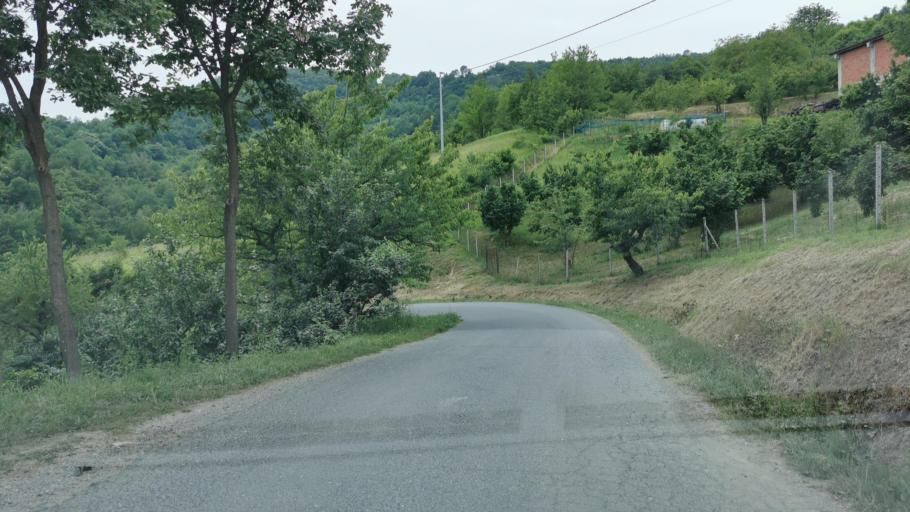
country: IT
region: Piedmont
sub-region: Provincia di Cuneo
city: Paroldo
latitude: 44.4289
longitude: 8.0567
